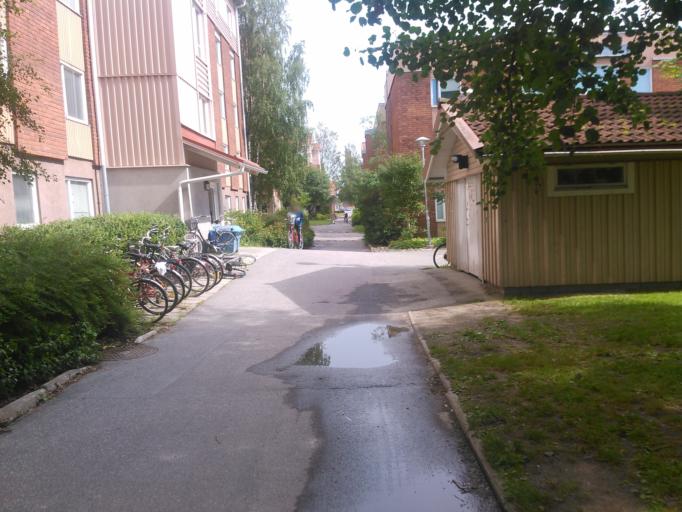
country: SE
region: Vaesterbotten
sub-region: Umea Kommun
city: Umea
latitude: 63.8129
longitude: 20.3102
